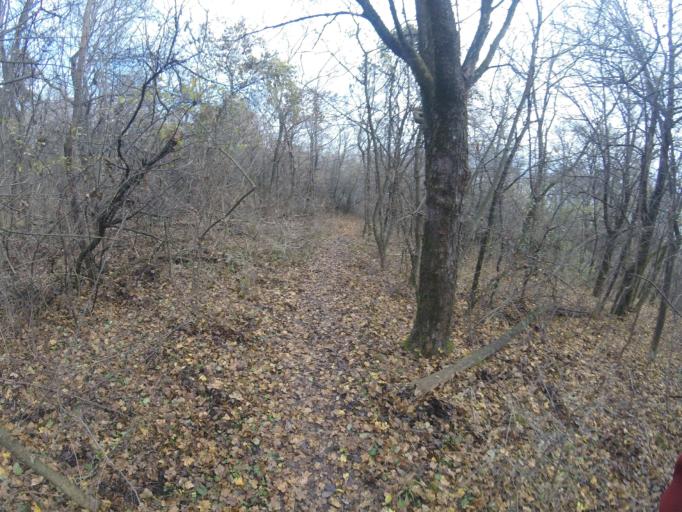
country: HU
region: Veszprem
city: Tihany
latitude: 46.8925
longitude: 17.8813
